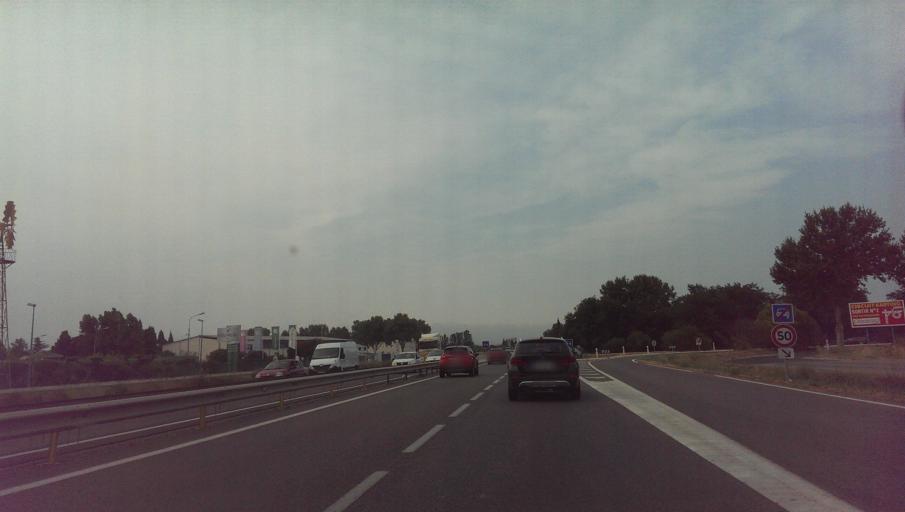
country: FR
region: Languedoc-Roussillon
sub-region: Departement des Pyrenees-Orientales
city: Rivesaltes
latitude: 42.7675
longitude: 2.8999
